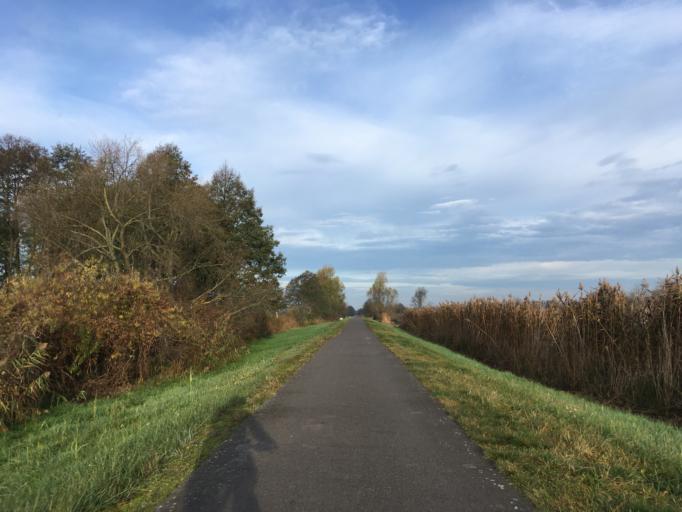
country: DE
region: Brandenburg
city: Luebben
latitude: 51.9059
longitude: 13.9266
